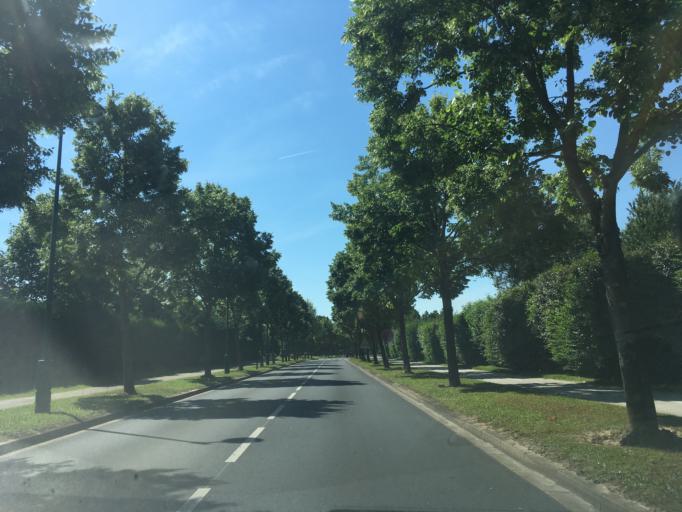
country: FR
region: Ile-de-France
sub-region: Departement de Seine-et-Marne
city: Magny-le-Hongre
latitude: 48.8585
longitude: 2.8141
